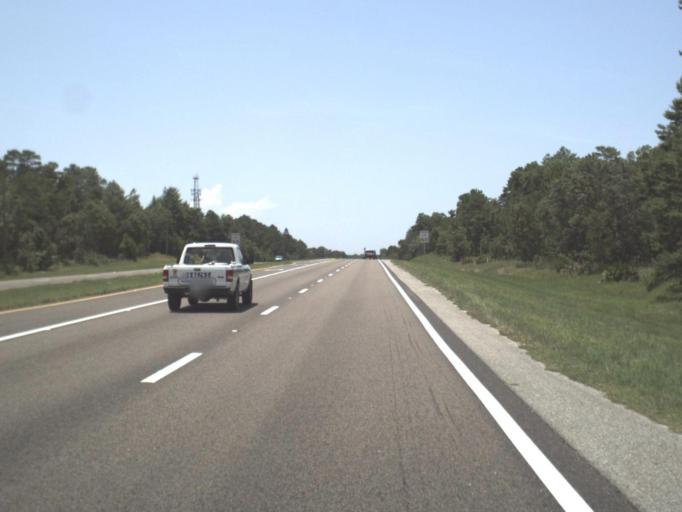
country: US
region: Florida
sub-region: Citrus County
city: Sugarmill Woods
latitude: 28.7130
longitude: -82.5353
